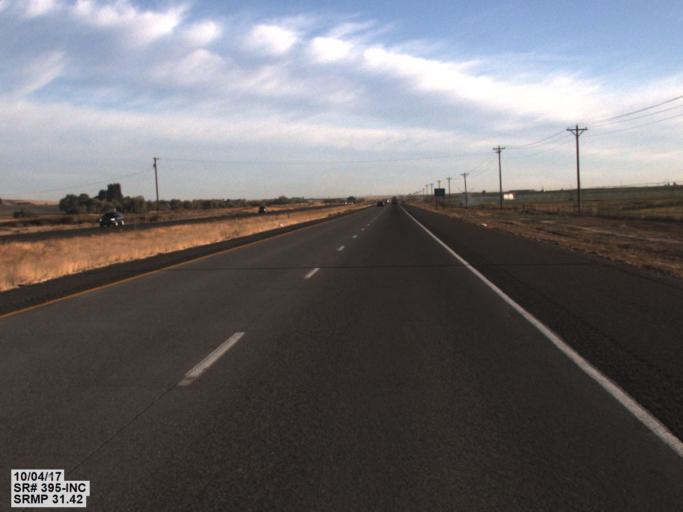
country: US
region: Washington
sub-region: Franklin County
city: Pasco
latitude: 46.3745
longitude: -119.0764
